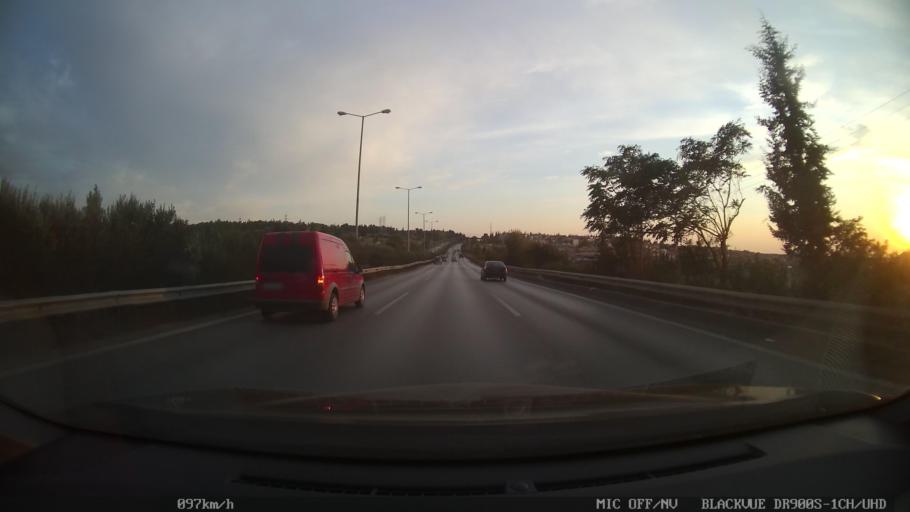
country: GR
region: Central Macedonia
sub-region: Nomos Thessalonikis
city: Pylaia
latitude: 40.6062
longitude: 22.9993
